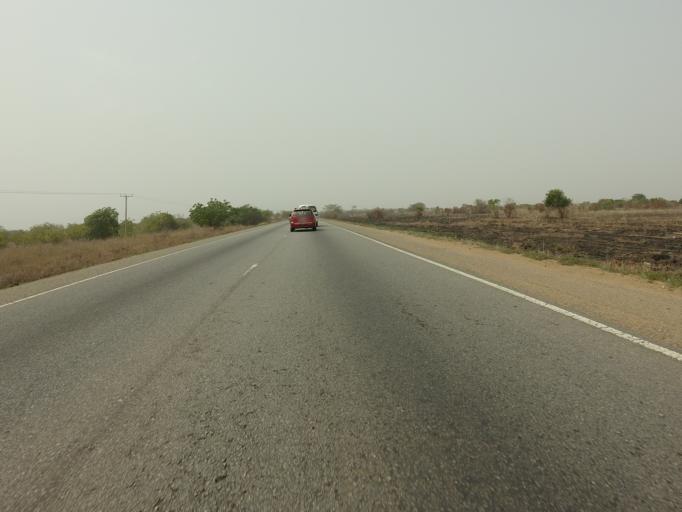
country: GH
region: Greater Accra
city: Tema
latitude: 5.8706
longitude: 0.3260
